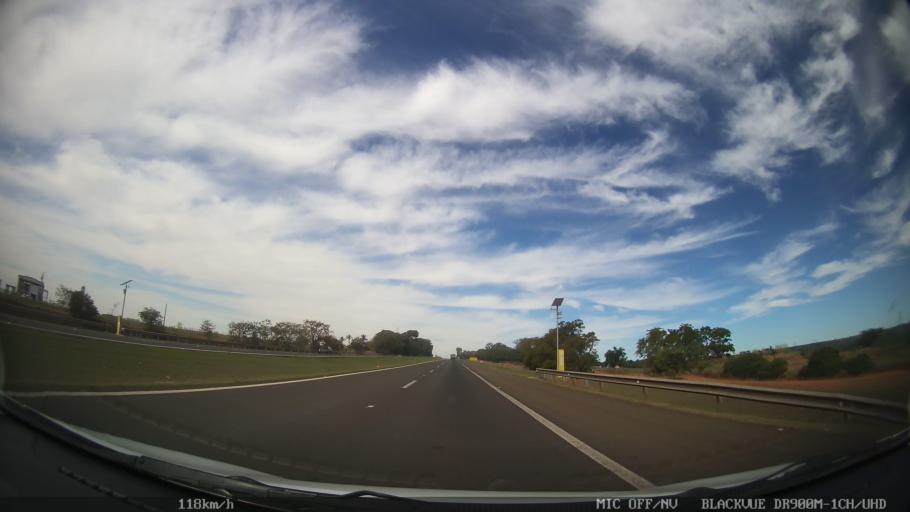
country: BR
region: Sao Paulo
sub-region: Matao
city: Matao
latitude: -21.5919
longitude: -48.4415
